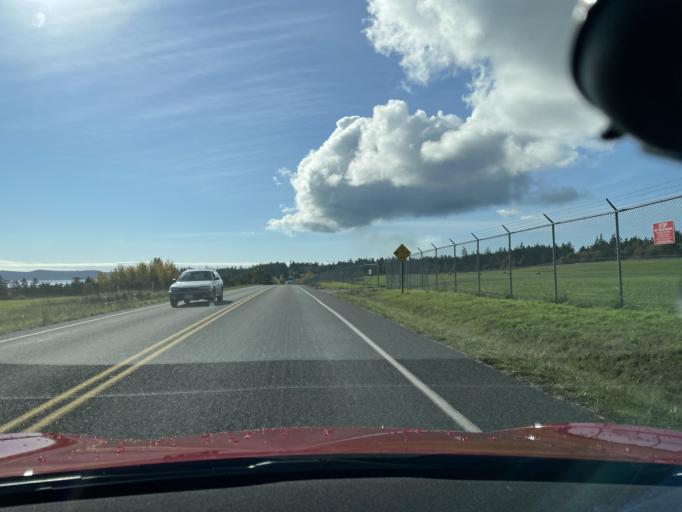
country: US
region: Washington
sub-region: San Juan County
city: Friday Harbor
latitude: 48.5200
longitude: -123.0231
